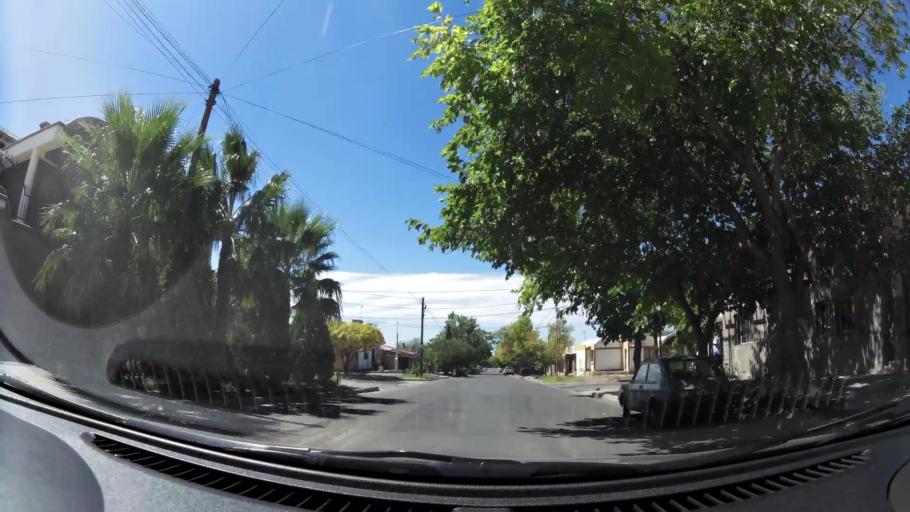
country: AR
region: Mendoza
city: Las Heras
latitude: -32.8377
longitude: -68.8689
